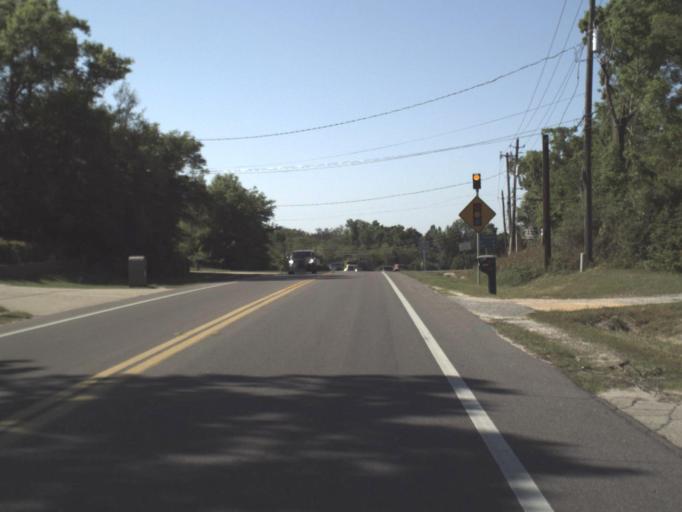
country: US
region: Florida
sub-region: Escambia County
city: Ferry Pass
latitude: 30.5397
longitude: -87.1954
